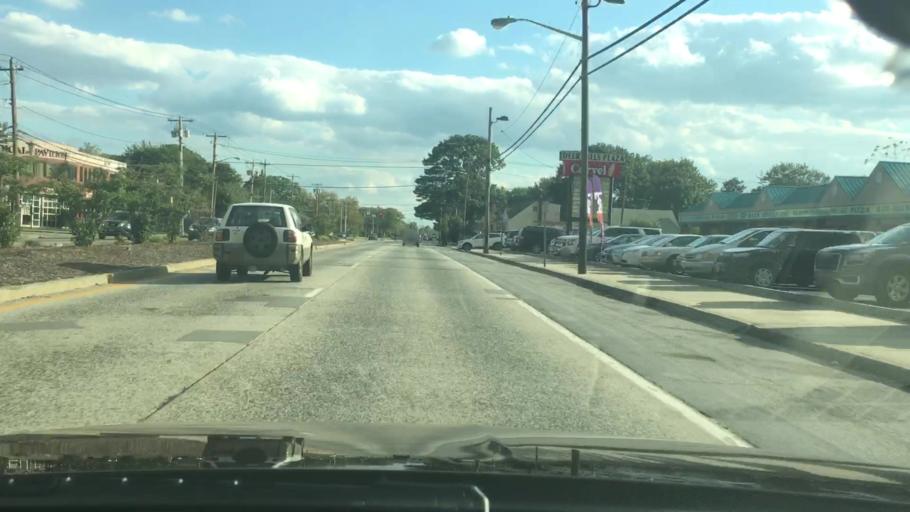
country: US
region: New York
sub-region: Suffolk County
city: Deer Park
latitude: 40.7737
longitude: -73.3345
